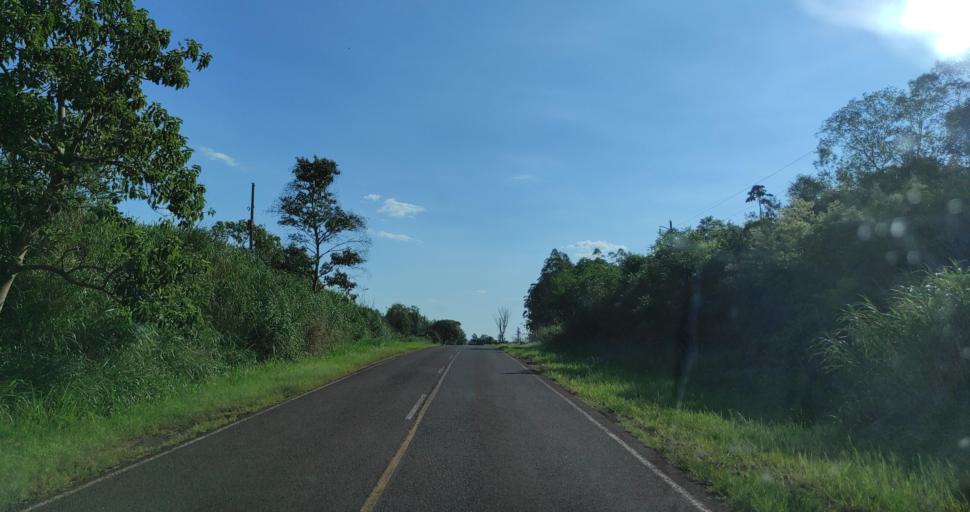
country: AR
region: Misiones
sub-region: Departamento de Eldorado
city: Eldorado
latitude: -26.3821
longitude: -54.3414
